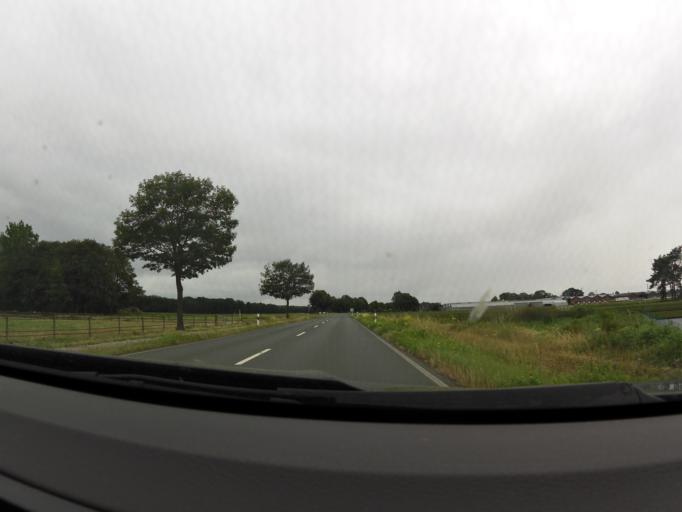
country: DE
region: North Rhine-Westphalia
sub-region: Regierungsbezirk Dusseldorf
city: Kevelaer
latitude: 51.5525
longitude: 6.2430
